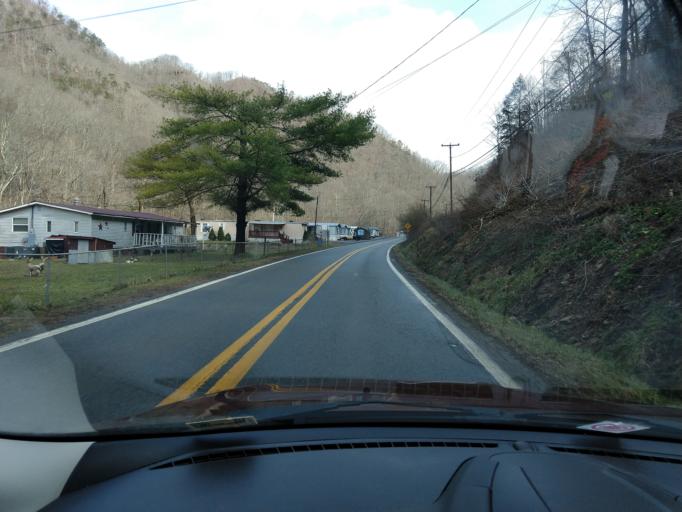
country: US
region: West Virginia
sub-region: McDowell County
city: Welch
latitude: 37.3458
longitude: -81.7872
